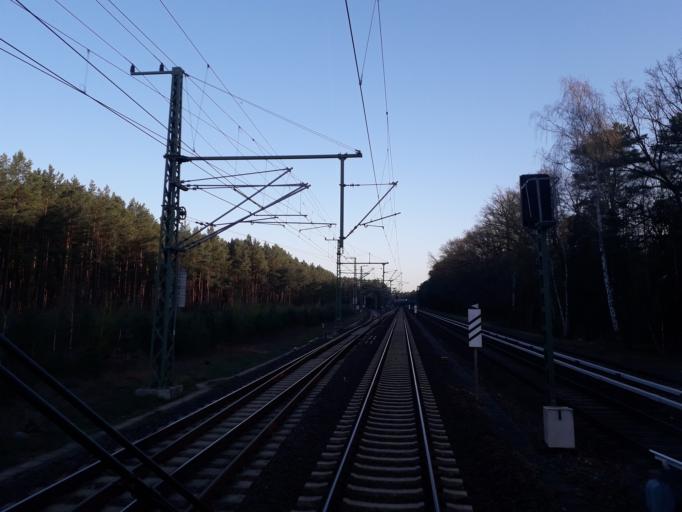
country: DE
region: Brandenburg
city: Zeuthen
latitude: 52.3874
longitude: 13.6048
